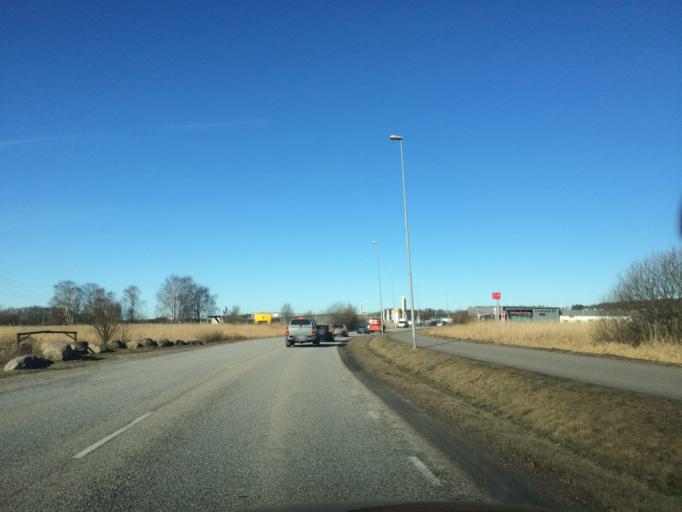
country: SE
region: Vaestra Goetaland
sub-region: Molndal
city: Moelndal
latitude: 57.6464
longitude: 11.9737
